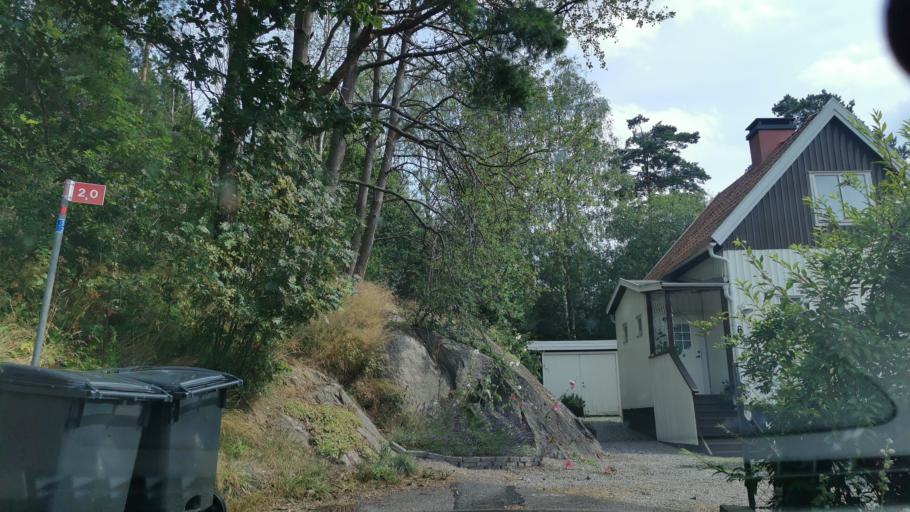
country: SE
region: Vaestra Goetaland
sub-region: Molndal
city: Moelndal
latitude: 57.6730
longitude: 11.9813
